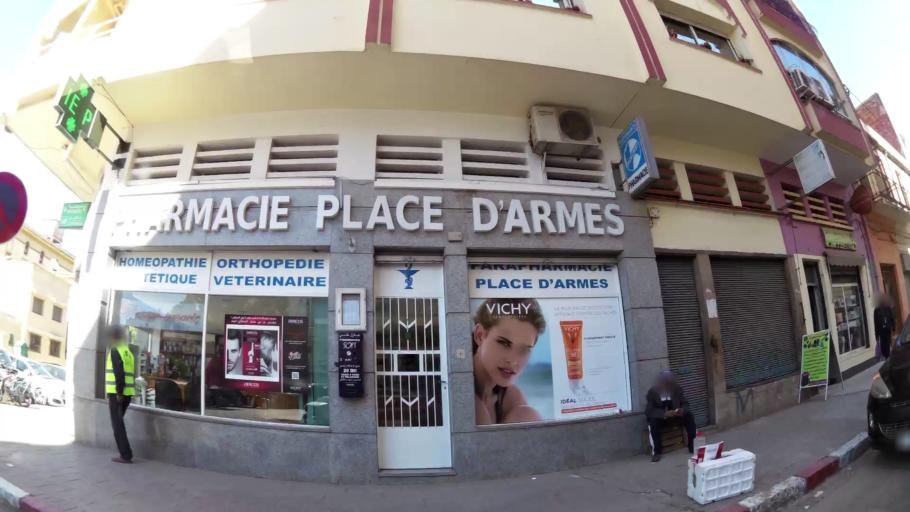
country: MA
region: Meknes-Tafilalet
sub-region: Meknes
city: Meknes
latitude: 33.8932
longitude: -5.5388
